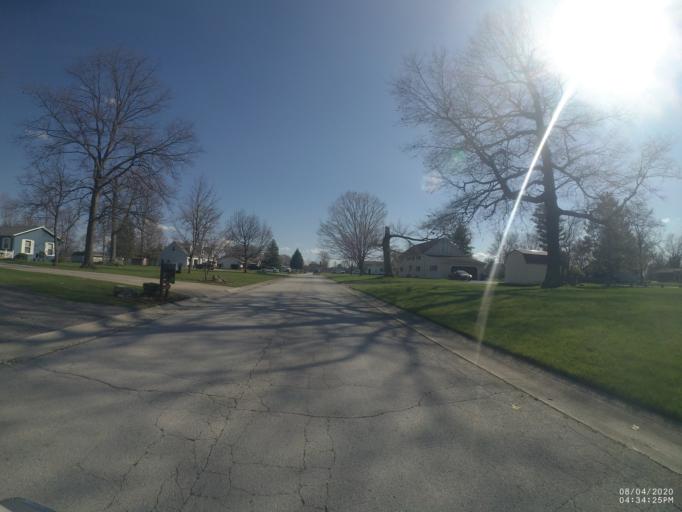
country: US
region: Ohio
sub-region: Sandusky County
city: Stony Prairie
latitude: 41.3328
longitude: -83.2033
